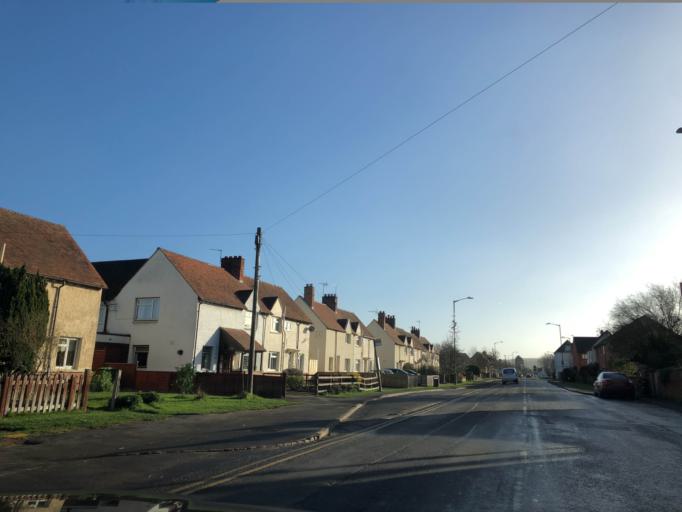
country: GB
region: England
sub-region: Warwickshire
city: Wellesbourne Mountford
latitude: 52.1974
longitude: -1.5932
